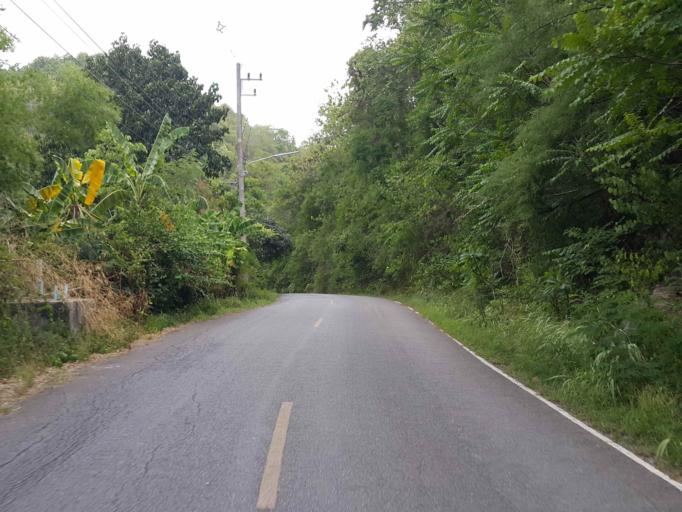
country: TH
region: Chiang Mai
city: Chiang Mai
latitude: 18.7618
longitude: 98.9202
